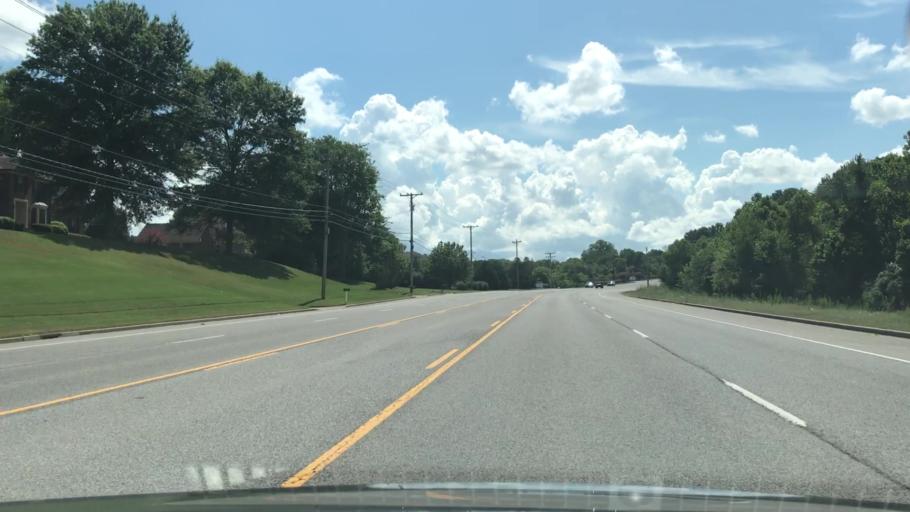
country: US
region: Tennessee
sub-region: Williamson County
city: Franklin
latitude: 35.9090
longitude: -86.8083
